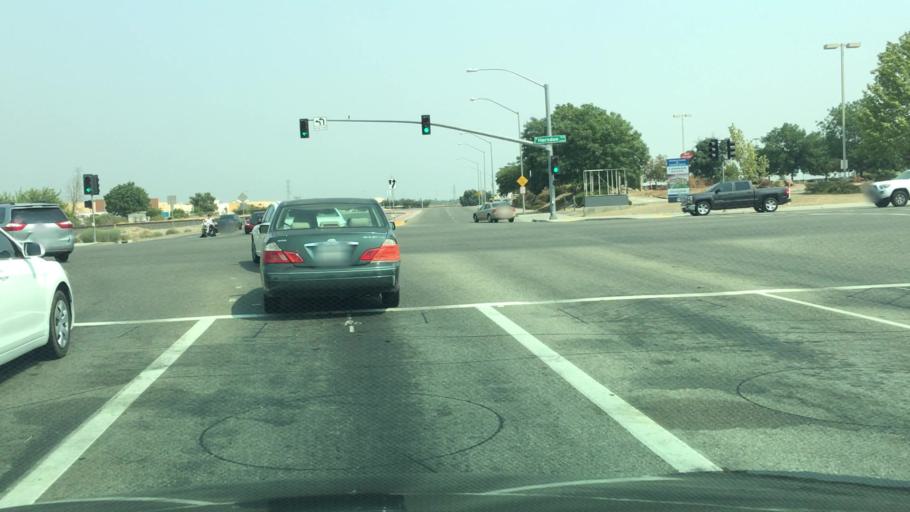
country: US
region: California
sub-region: Fresno County
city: Biola
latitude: 36.8342
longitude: -119.9160
